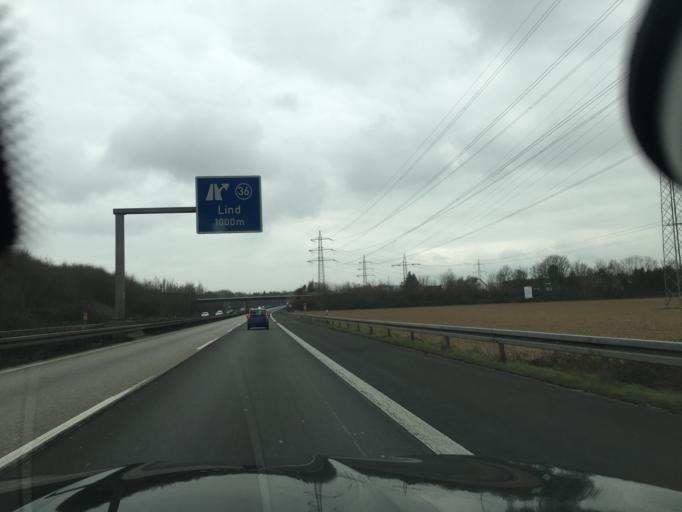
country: DE
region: North Rhine-Westphalia
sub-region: Regierungsbezirk Koln
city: Wahn-Heide
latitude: 50.8538
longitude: 7.0974
